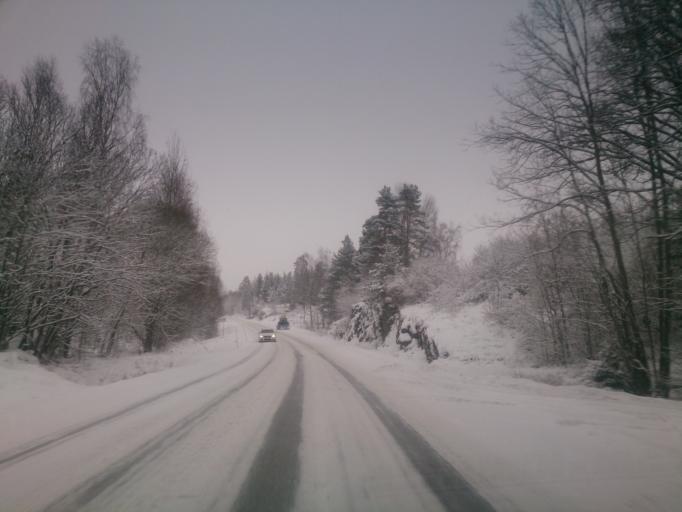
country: SE
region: OEstergoetland
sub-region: Finspangs Kommun
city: Finspang
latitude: 58.6217
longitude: 15.8173
